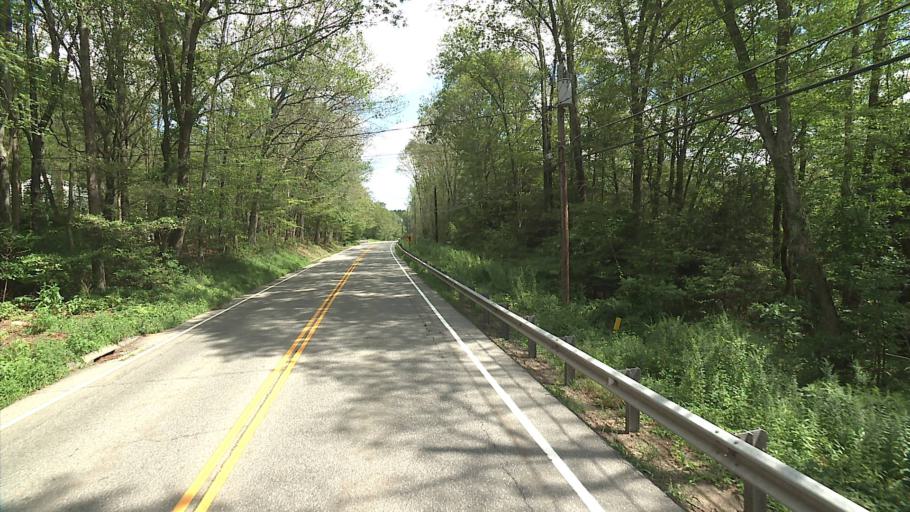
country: US
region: Connecticut
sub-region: Windham County
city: Windham
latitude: 41.8222
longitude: -72.1052
